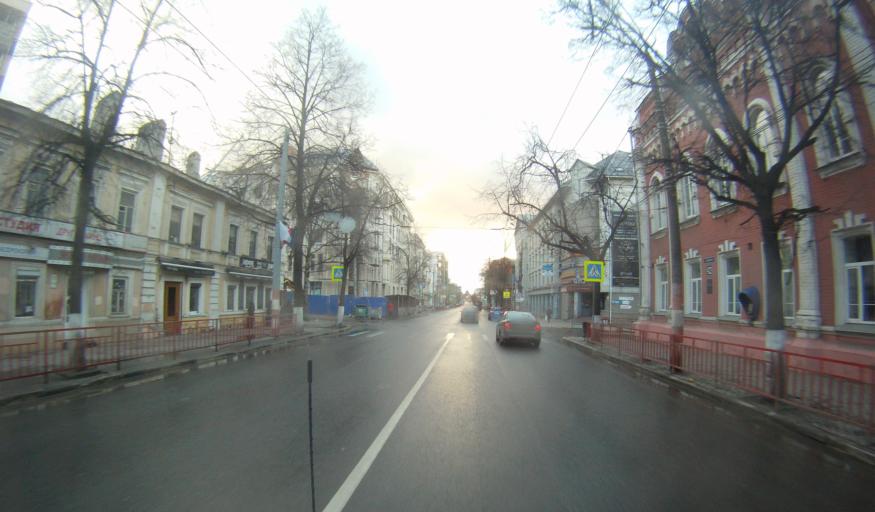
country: RU
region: Nizjnij Novgorod
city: Nizhniy Novgorod
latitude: 56.3196
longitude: 44.0143
